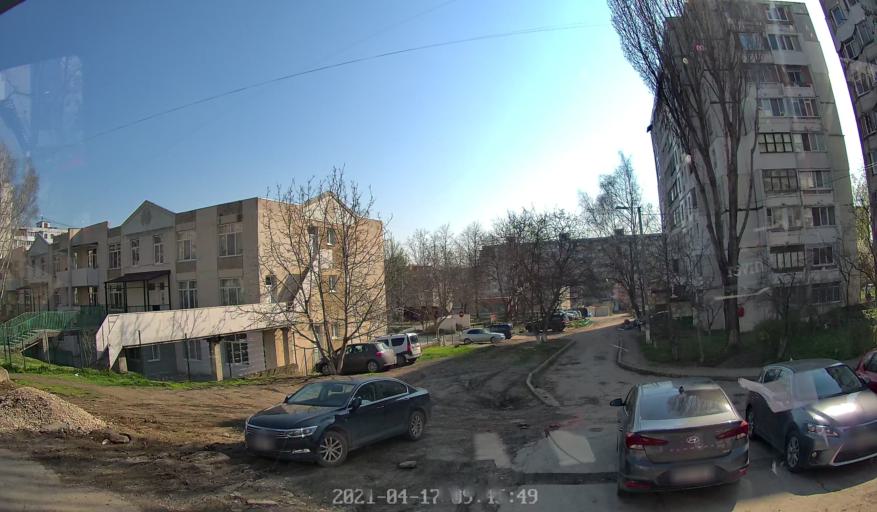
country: MD
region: Chisinau
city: Stauceni
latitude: 47.0514
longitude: 28.8864
